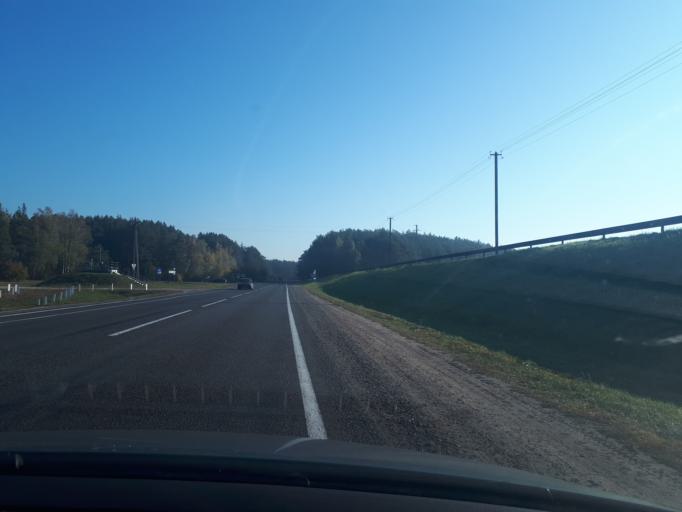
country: BY
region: Grodnenskaya
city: Zel'va
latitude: 53.1459
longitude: 24.8403
